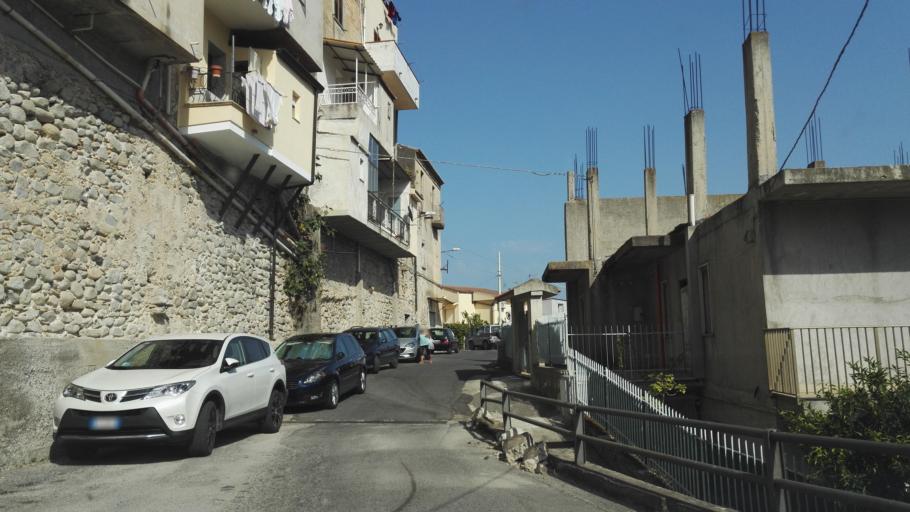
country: IT
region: Calabria
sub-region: Provincia di Reggio Calabria
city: Monasterace
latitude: 38.4529
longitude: 16.5516
